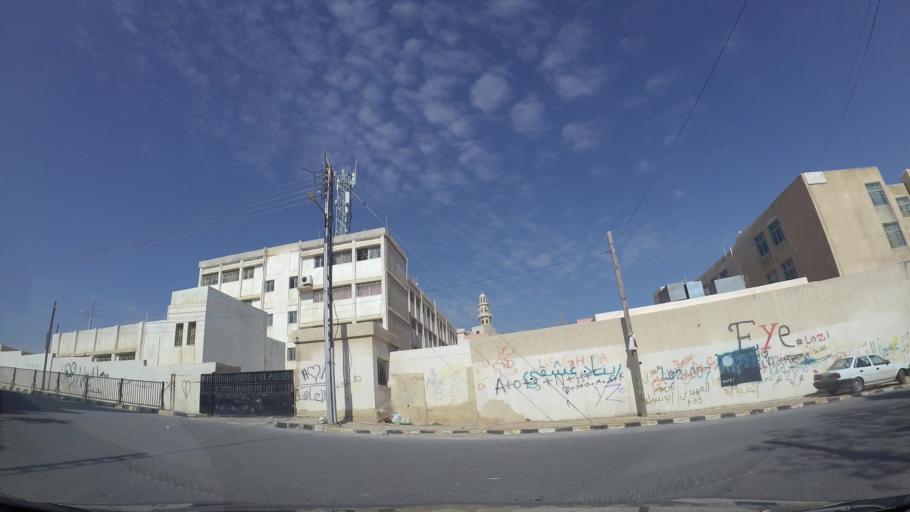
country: JO
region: Amman
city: Al Jubayhah
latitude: 31.9982
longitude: 35.8927
